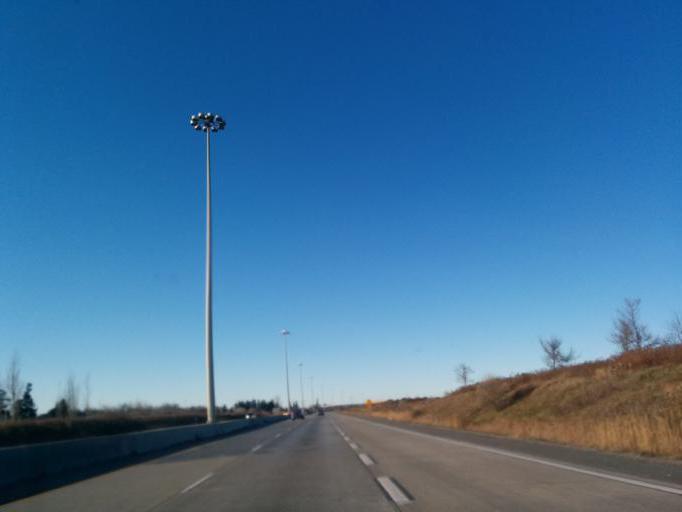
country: CA
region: Ontario
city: Brampton
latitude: 43.7386
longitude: -79.7785
